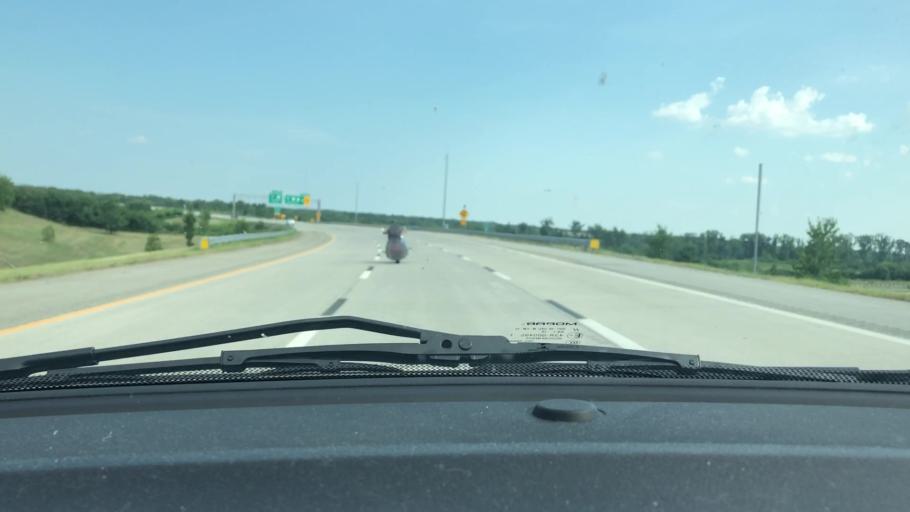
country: US
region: North Carolina
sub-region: Guilford County
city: Jamestown
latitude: 36.0071
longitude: -79.8527
